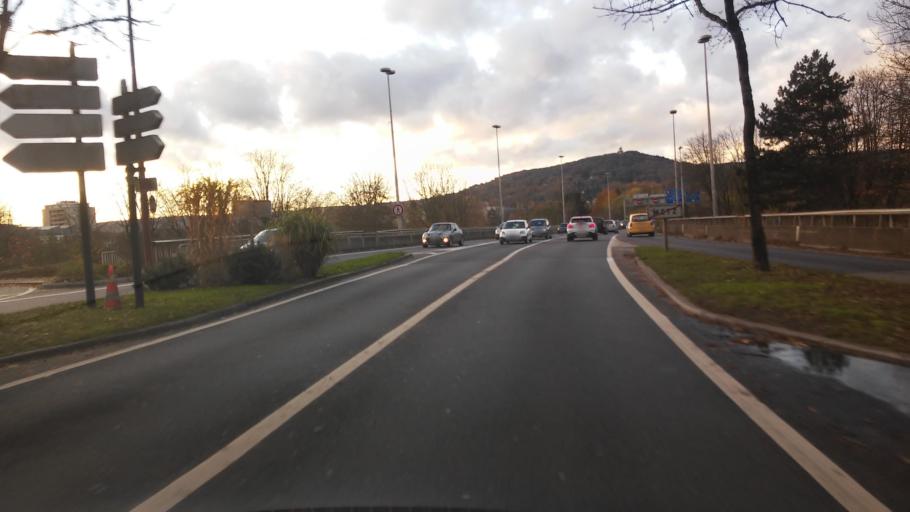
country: FR
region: Lorraine
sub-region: Departement de la Moselle
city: Metz
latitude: 49.1127
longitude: 6.1668
